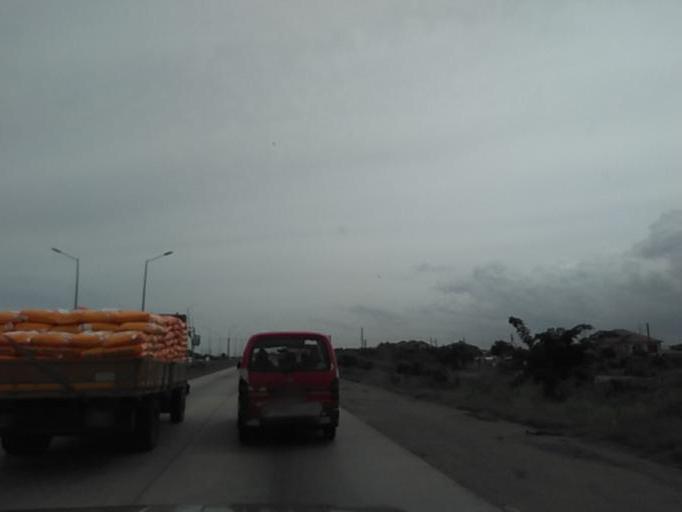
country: GH
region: Greater Accra
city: Nungua
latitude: 5.6556
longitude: -0.0923
